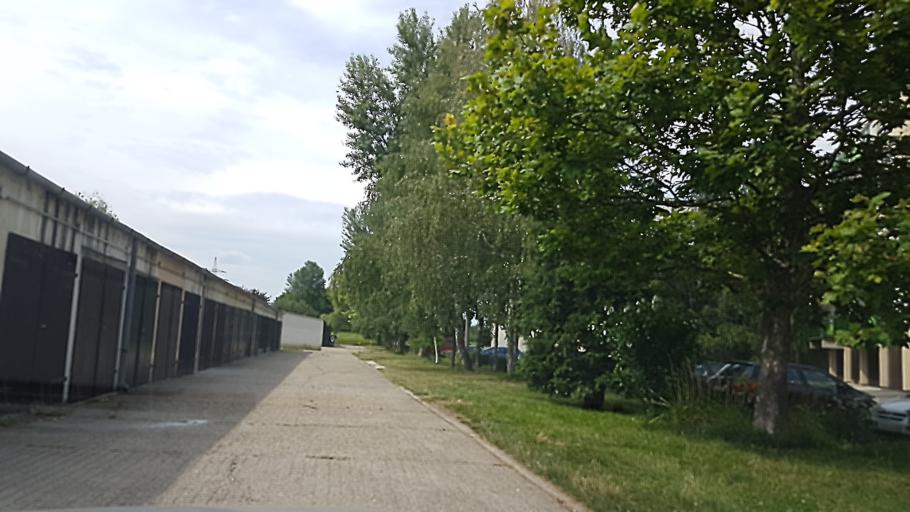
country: HU
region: Gyor-Moson-Sopron
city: Sopron
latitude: 47.6942
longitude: 16.5707
